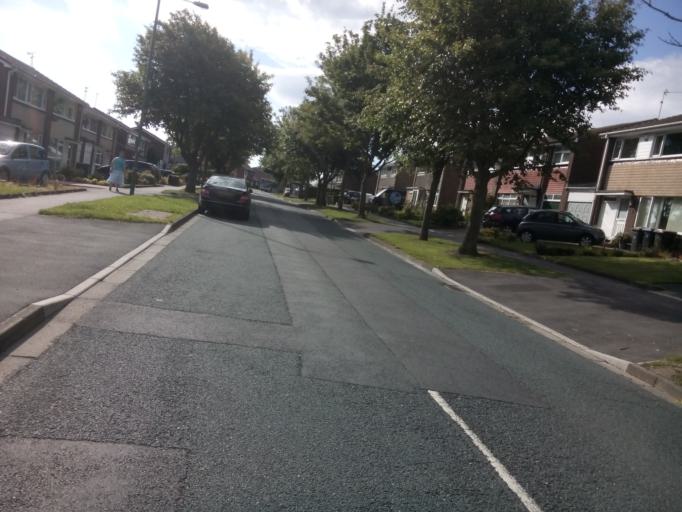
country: GB
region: England
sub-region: County Durham
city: Durham
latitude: 54.8028
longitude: -1.5652
